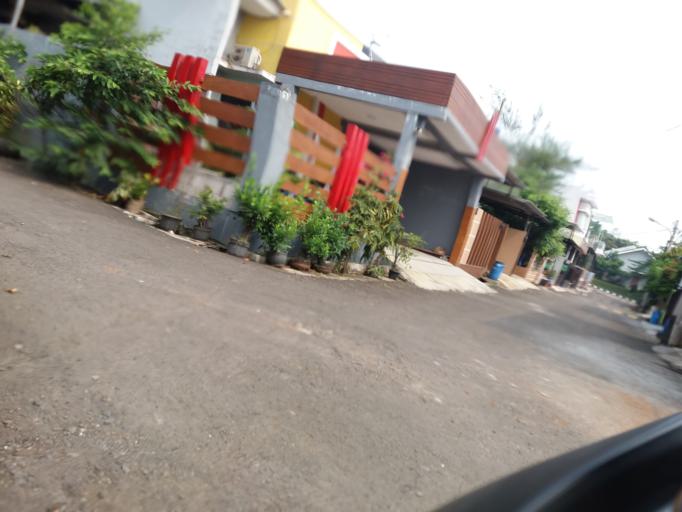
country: ID
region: West Java
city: Cibinong
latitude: -6.4360
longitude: 106.8651
